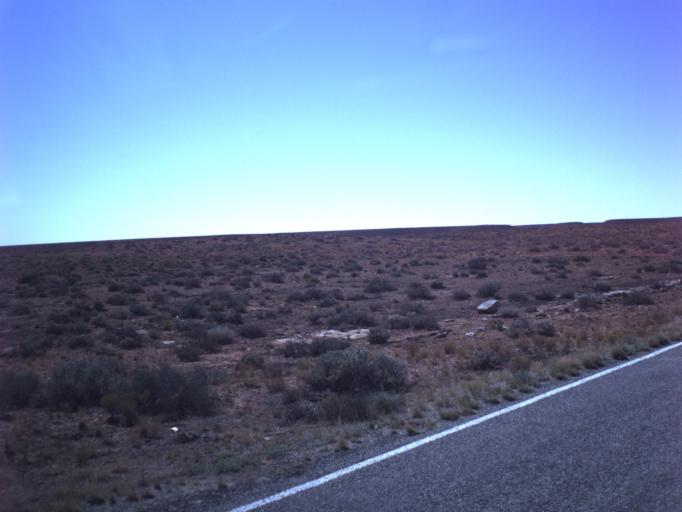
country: US
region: Utah
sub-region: San Juan County
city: Blanding
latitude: 37.2002
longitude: -109.8911
